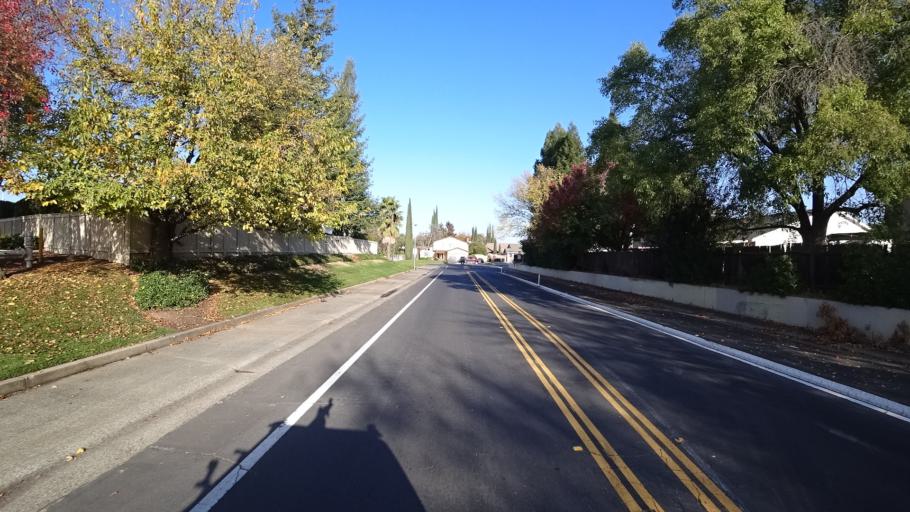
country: US
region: California
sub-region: Sacramento County
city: Citrus Heights
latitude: 38.6948
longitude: -121.2694
